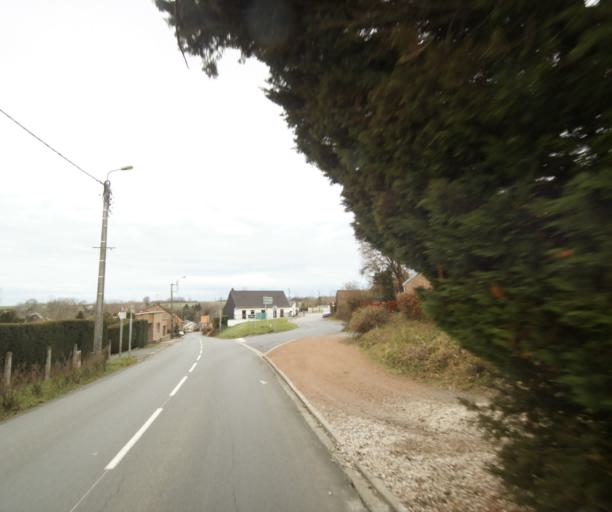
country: FR
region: Nord-Pas-de-Calais
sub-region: Departement du Nord
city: Sebourg
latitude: 50.3338
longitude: 3.6540
